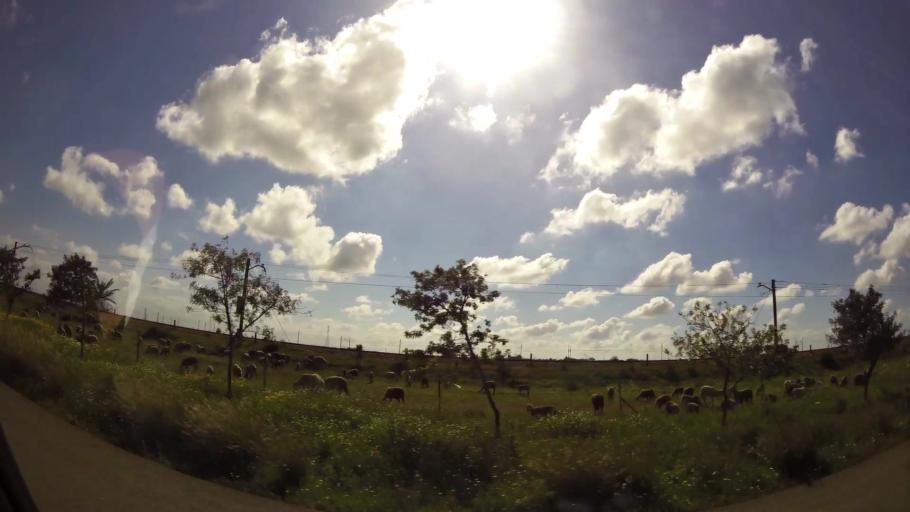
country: MA
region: Chaouia-Ouardigha
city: Nouaseur
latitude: 33.4046
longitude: -7.6237
